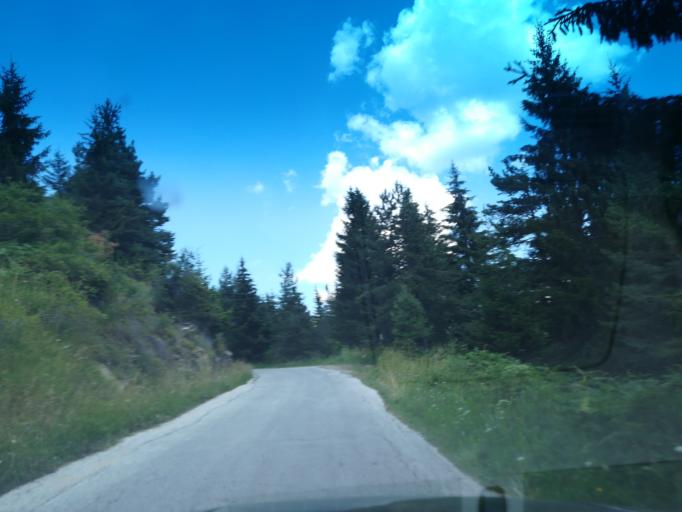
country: BG
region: Smolyan
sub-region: Obshtina Chepelare
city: Chepelare
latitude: 41.6766
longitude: 24.7701
